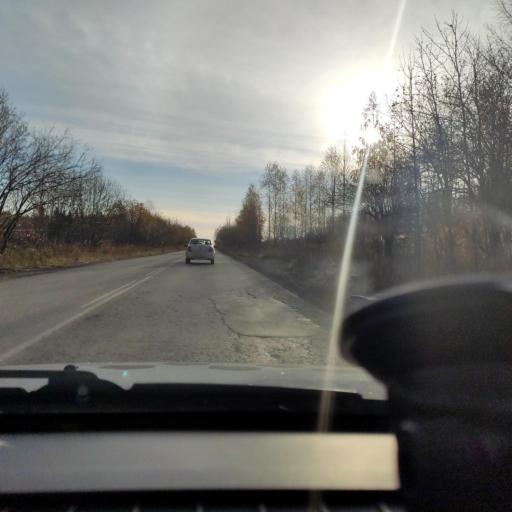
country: RU
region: Perm
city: Ferma
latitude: 57.9463
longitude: 56.4132
